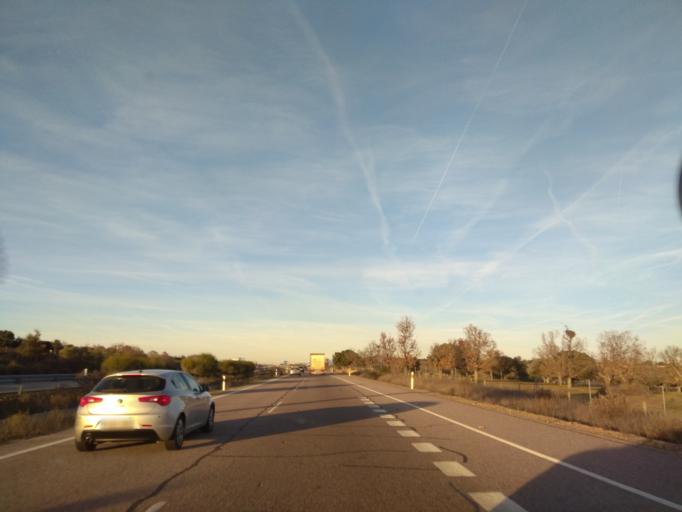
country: ES
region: Castille and Leon
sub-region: Provincia de Salamanca
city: Tenebron
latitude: 40.6721
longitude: -6.4306
